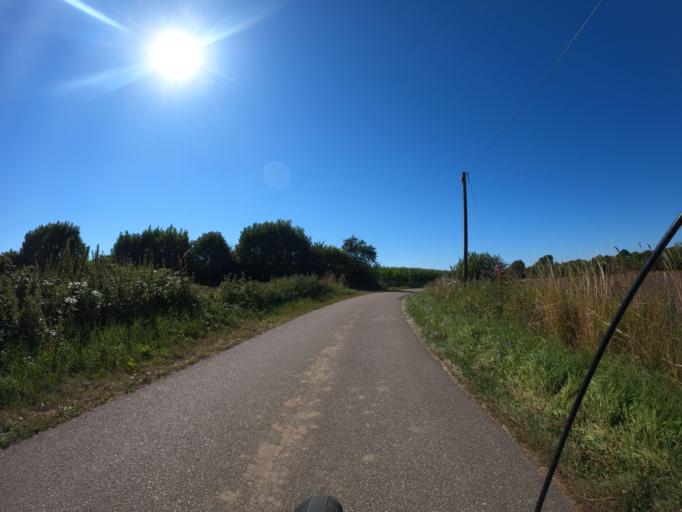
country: DE
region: Schleswig-Holstein
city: Steinberg
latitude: 54.7776
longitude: 9.7631
